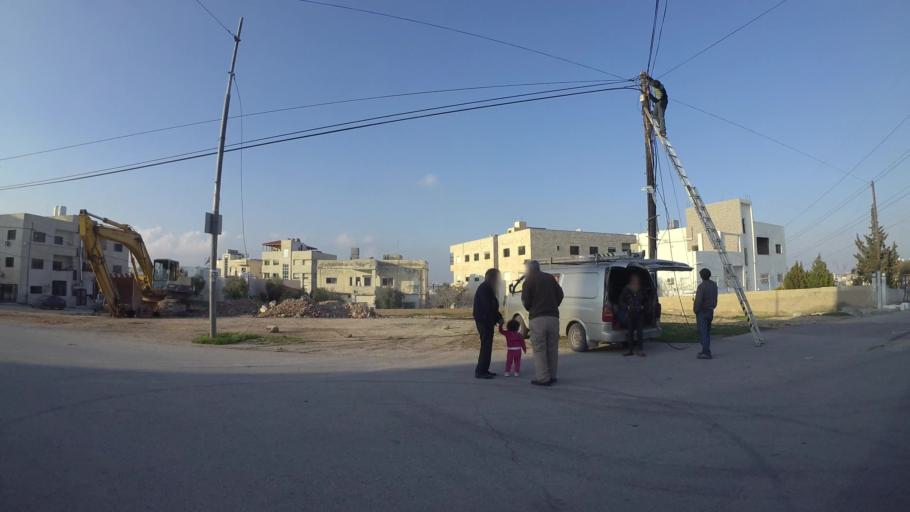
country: JO
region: Amman
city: Amman
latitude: 31.9842
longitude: 35.9678
